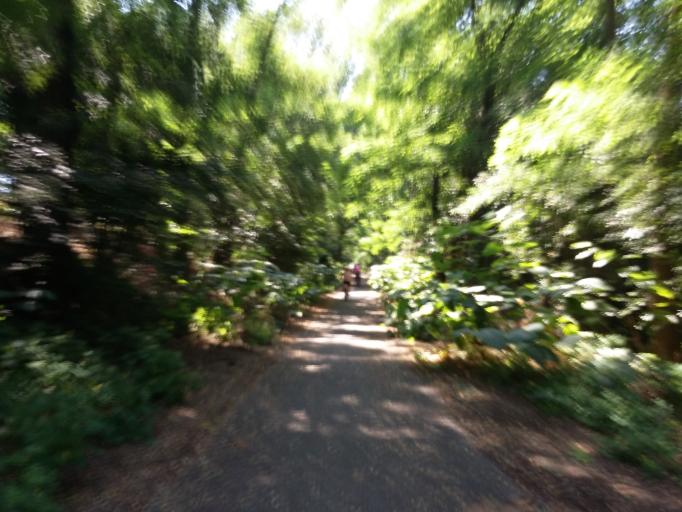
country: AT
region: Lower Austria
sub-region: Politischer Bezirk Ganserndorf
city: Marchegg
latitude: 48.2683
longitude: 16.9606
